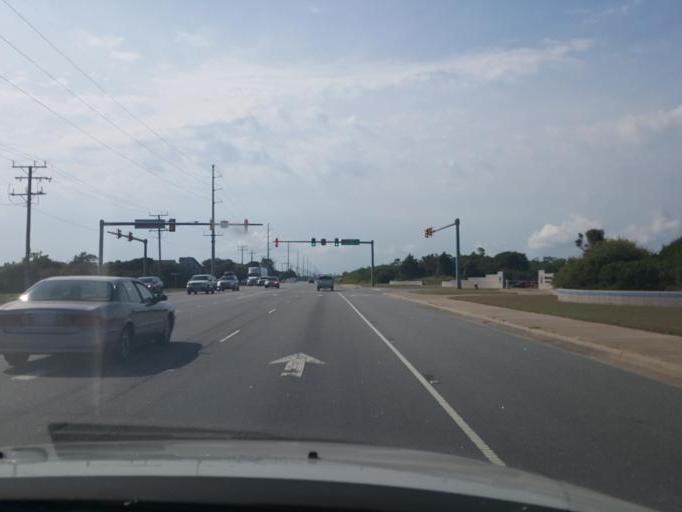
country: US
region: North Carolina
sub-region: Dare County
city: Kill Devil Hills
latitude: 36.0209
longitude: -75.6654
